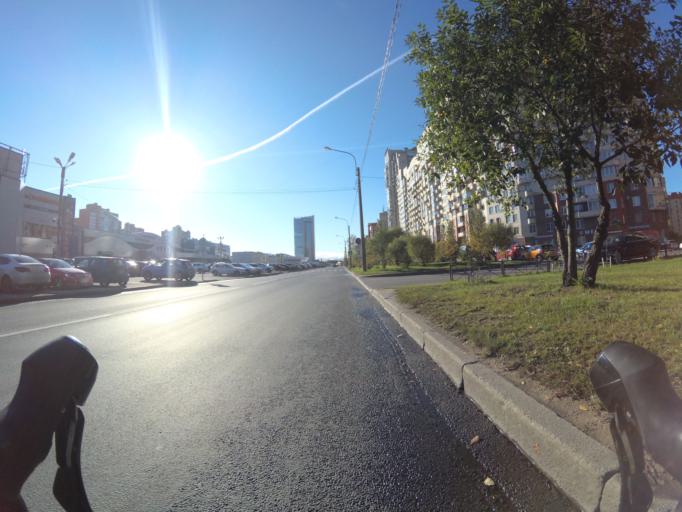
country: RU
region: Leningrad
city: Untolovo
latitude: 59.9914
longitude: 30.2040
